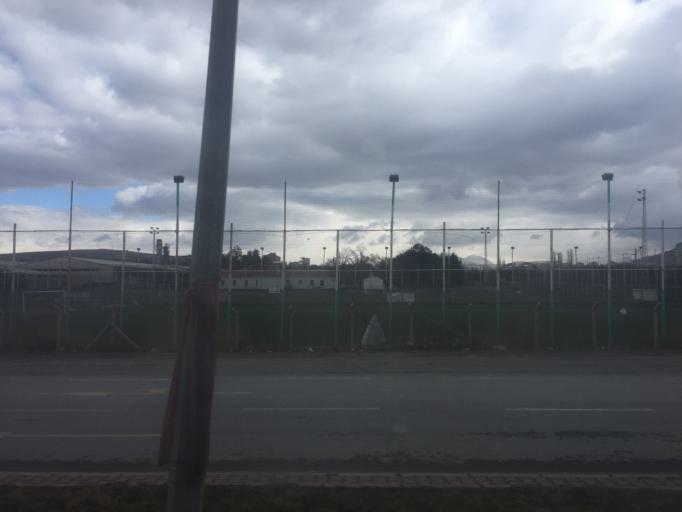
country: TR
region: Kayseri
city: Melikgazi
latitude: 38.7511
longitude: 35.4057
